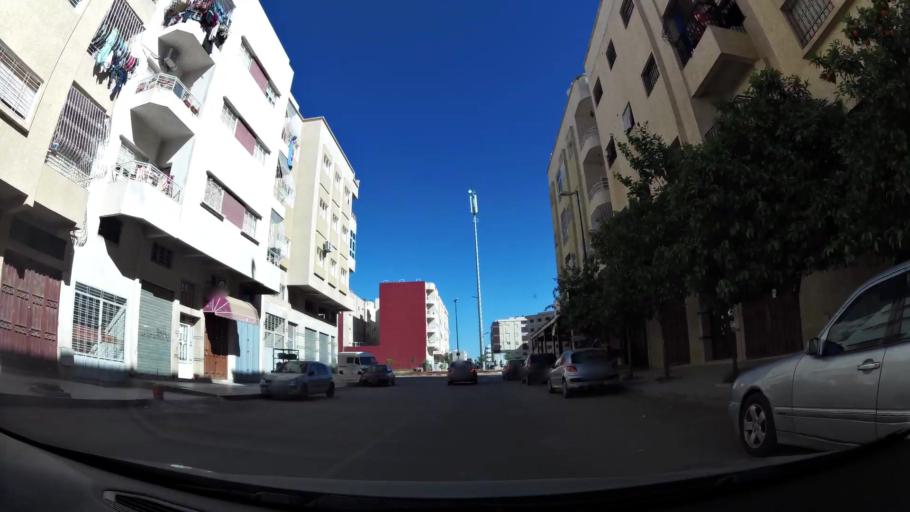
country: MA
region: Fes-Boulemane
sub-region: Fes
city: Fes
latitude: 34.0155
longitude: -4.9631
